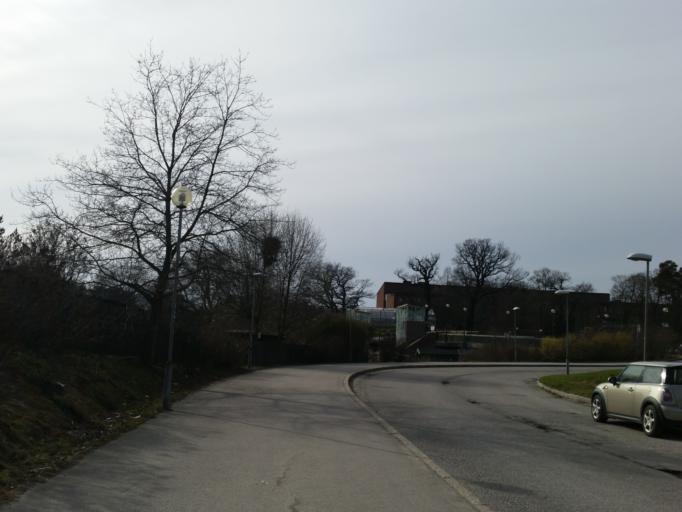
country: SE
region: Stockholm
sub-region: Norrtalje Kommun
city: Bergshamra
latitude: 59.3652
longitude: 18.0526
